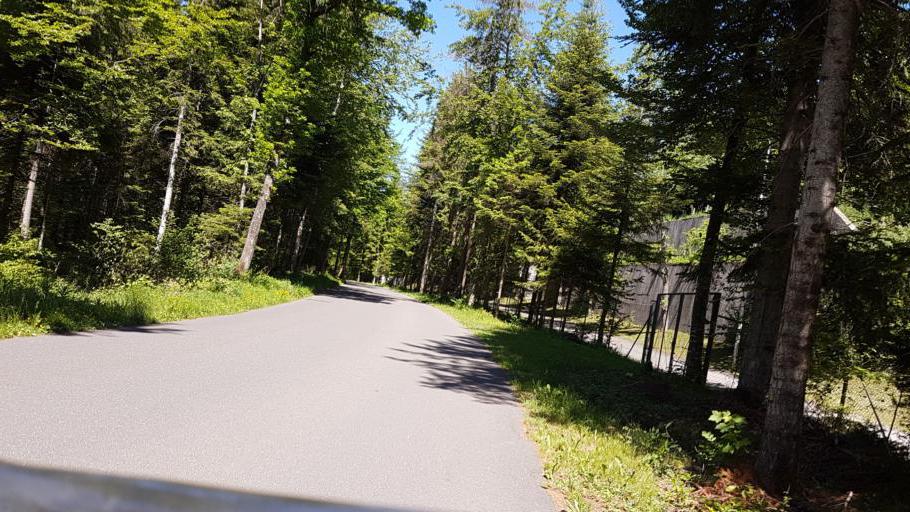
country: CH
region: Bern
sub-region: Thun District
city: Thun
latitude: 46.7268
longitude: 7.5994
